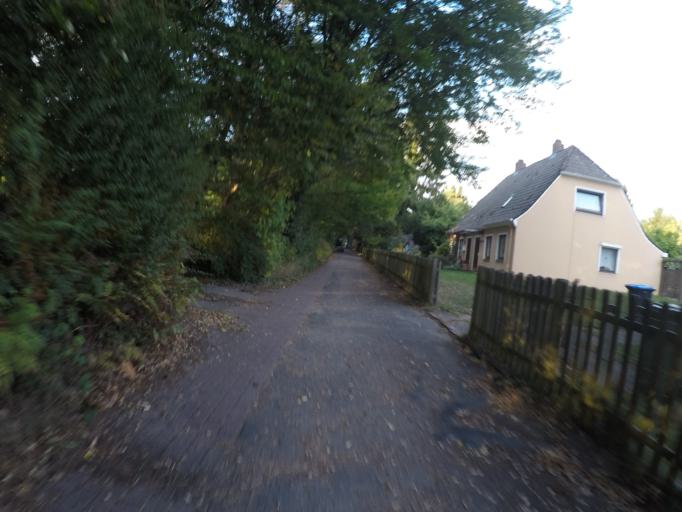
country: DE
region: Hamburg
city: Farmsen-Berne
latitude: 53.6311
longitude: 10.1428
